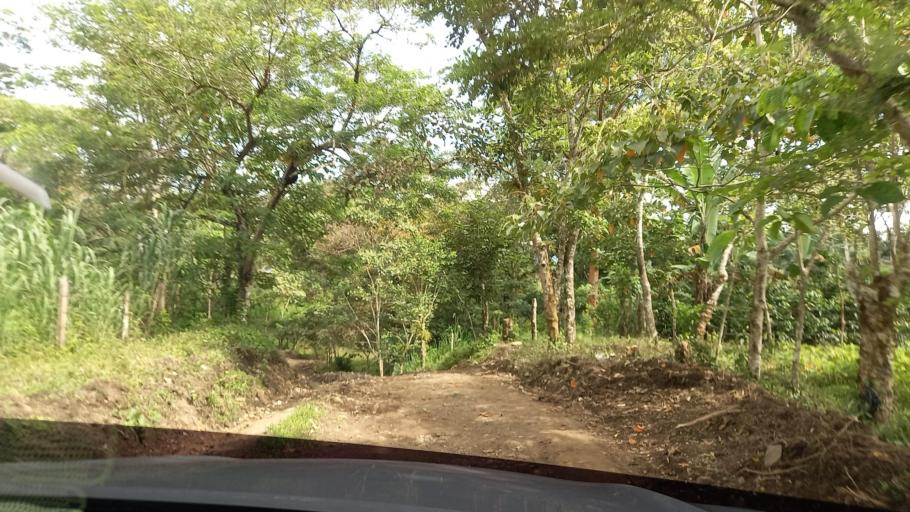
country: NI
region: Jinotega
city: San Jose de Bocay
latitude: 13.3880
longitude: -85.6896
